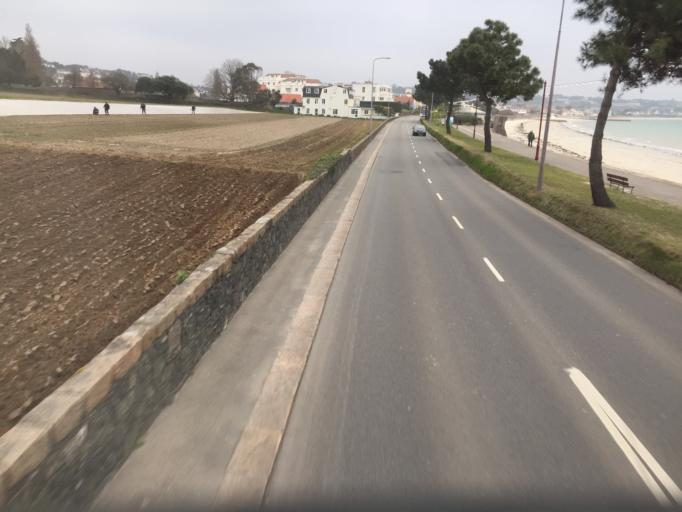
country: JE
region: St Helier
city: Saint Helier
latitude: 49.1930
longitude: -2.1660
